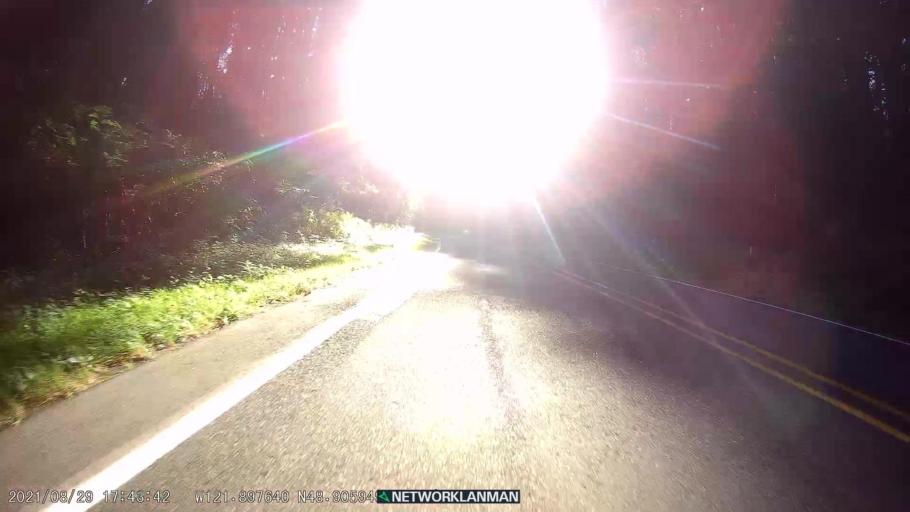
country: US
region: Washington
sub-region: Whatcom County
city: Peaceful Valley
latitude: 48.9060
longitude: -121.8975
